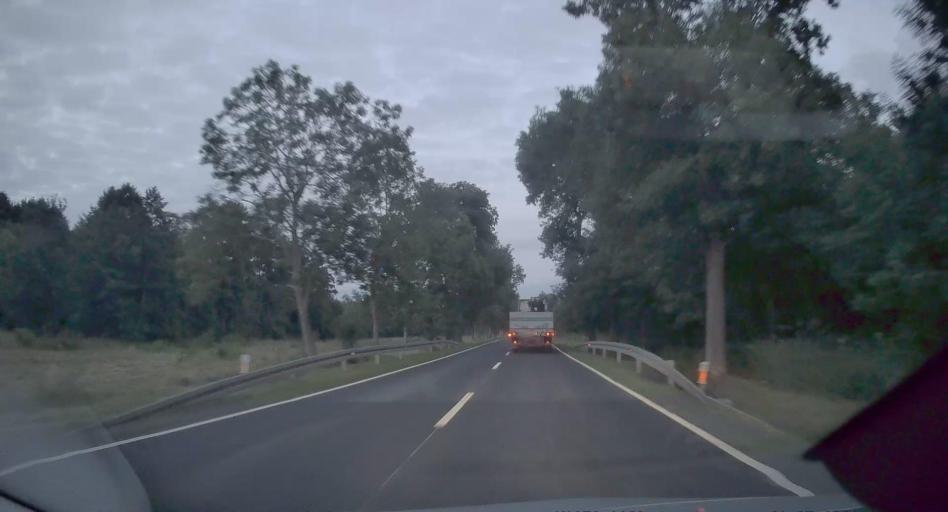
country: PL
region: Silesian Voivodeship
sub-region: Powiat klobucki
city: Opatow
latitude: 50.9578
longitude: 18.7833
